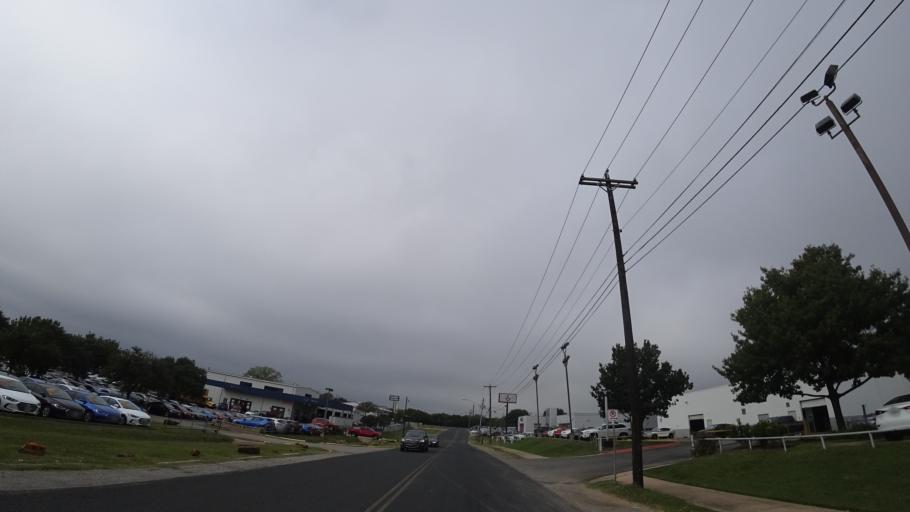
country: US
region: Texas
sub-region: Travis County
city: Austin
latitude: 30.2101
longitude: -97.7563
